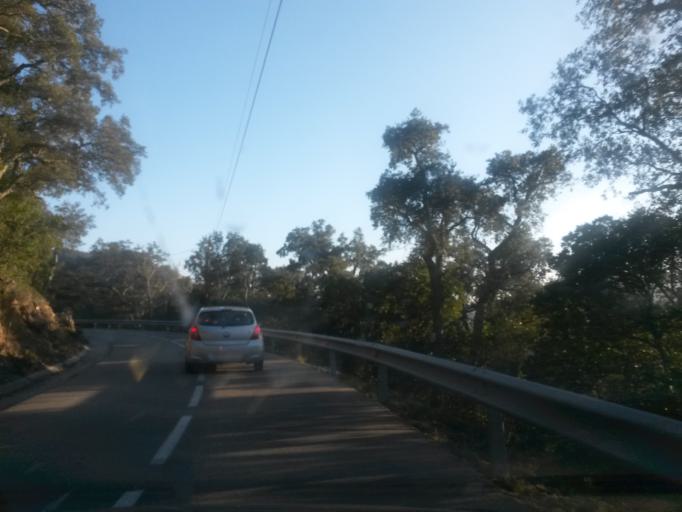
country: ES
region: Catalonia
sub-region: Provincia de Girona
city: Darnius
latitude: 42.3755
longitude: 2.7987
